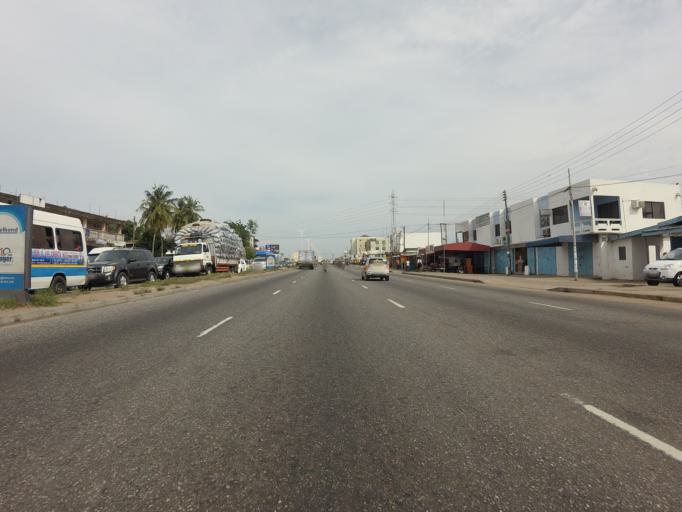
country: GH
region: Greater Accra
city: Dome
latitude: 5.6222
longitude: -0.2318
